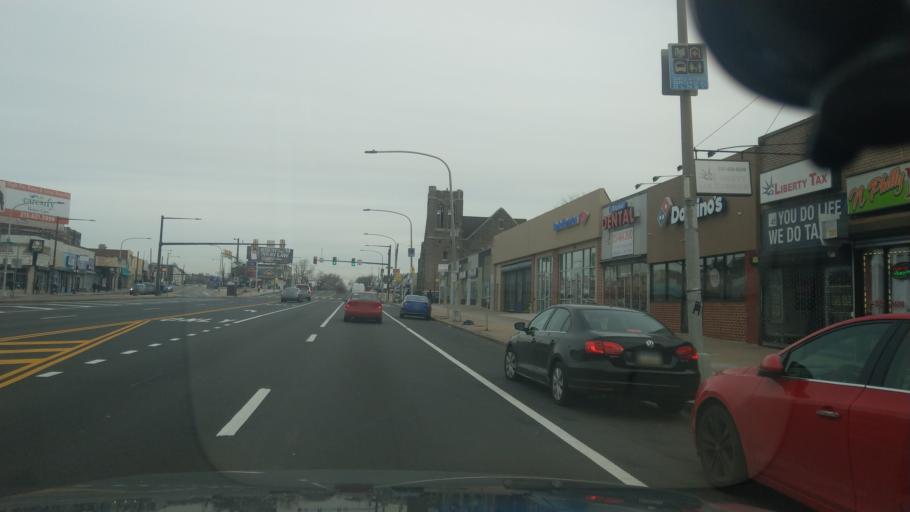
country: US
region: Pennsylvania
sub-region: Montgomery County
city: Wyncote
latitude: 40.0405
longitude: -75.1443
